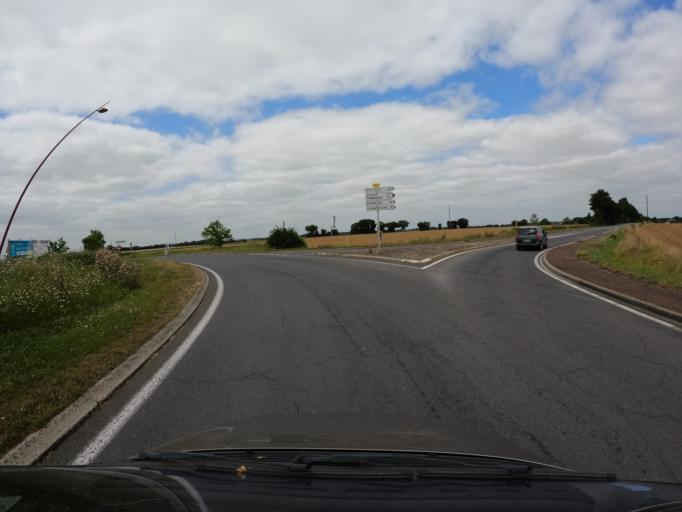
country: FR
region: Poitou-Charentes
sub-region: Departement de la Vienne
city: Civray
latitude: 46.1629
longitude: 0.2992
